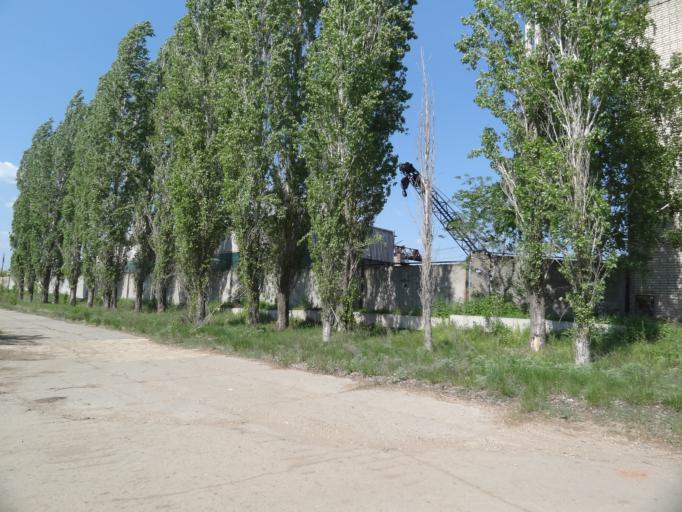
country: RU
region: Saratov
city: Privolzhskiy
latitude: 51.3936
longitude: 46.0798
